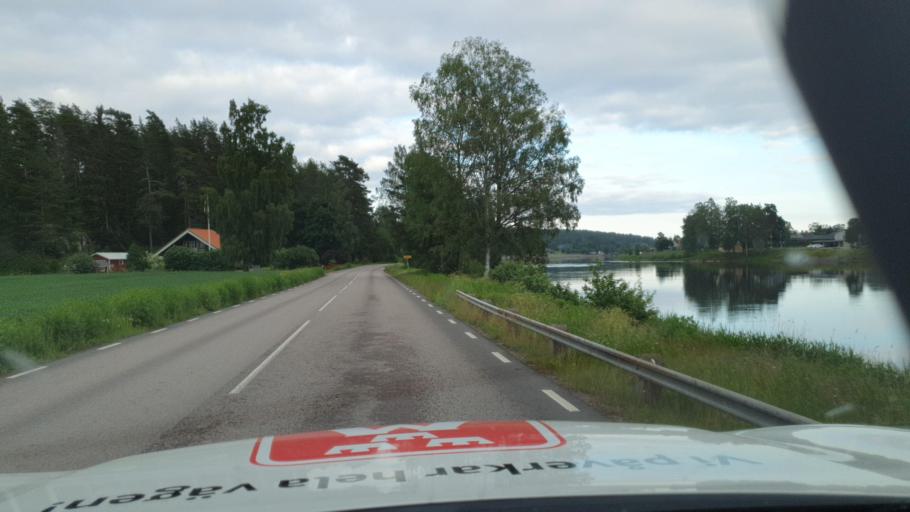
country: SE
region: Vaermland
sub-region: Karlstads Kommun
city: Karlstad
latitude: 59.4256
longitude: 13.4702
